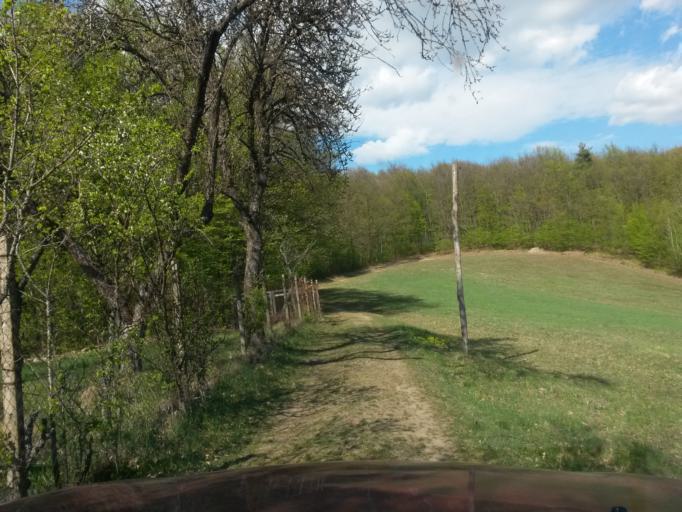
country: SK
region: Presovsky
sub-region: Okres Presov
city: Presov
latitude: 48.9401
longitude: 21.1215
